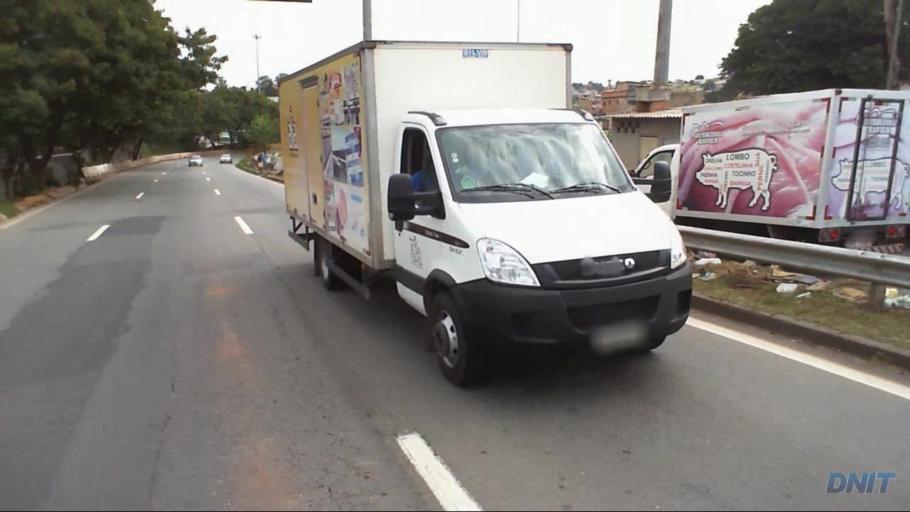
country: BR
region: Minas Gerais
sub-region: Belo Horizonte
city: Belo Horizonte
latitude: -19.8568
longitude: -43.8954
